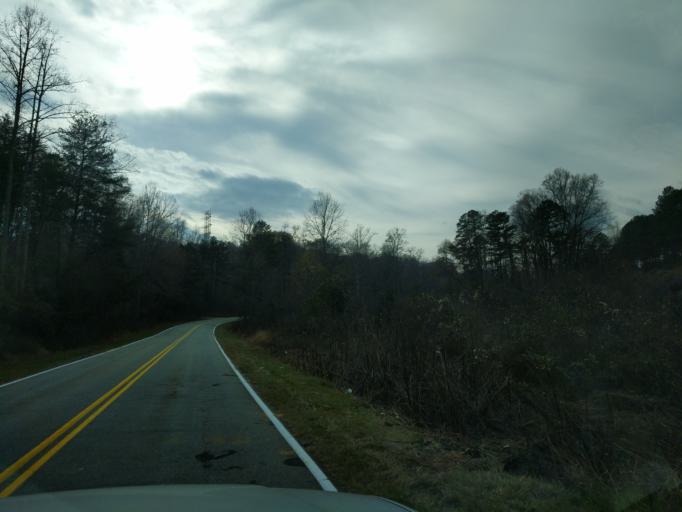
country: US
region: South Carolina
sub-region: Pickens County
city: Clemson
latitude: 34.7881
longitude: -82.8876
